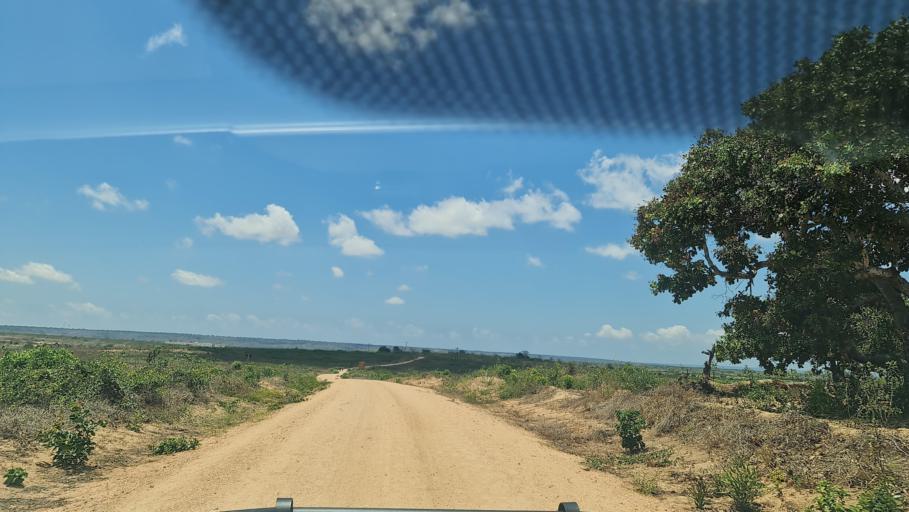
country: MZ
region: Nampula
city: Nacala
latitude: -14.3293
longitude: 40.5954
